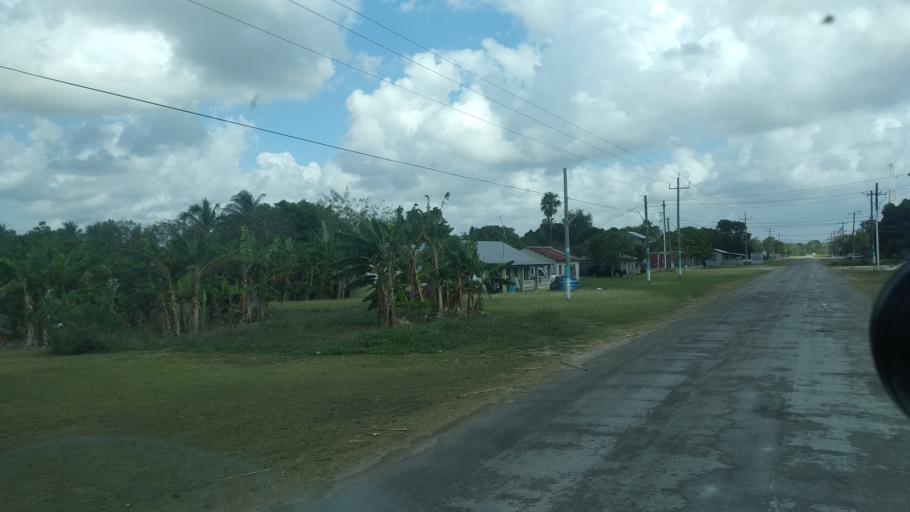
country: BZ
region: Corozal
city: Corozal
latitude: 18.3485
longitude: -88.4978
